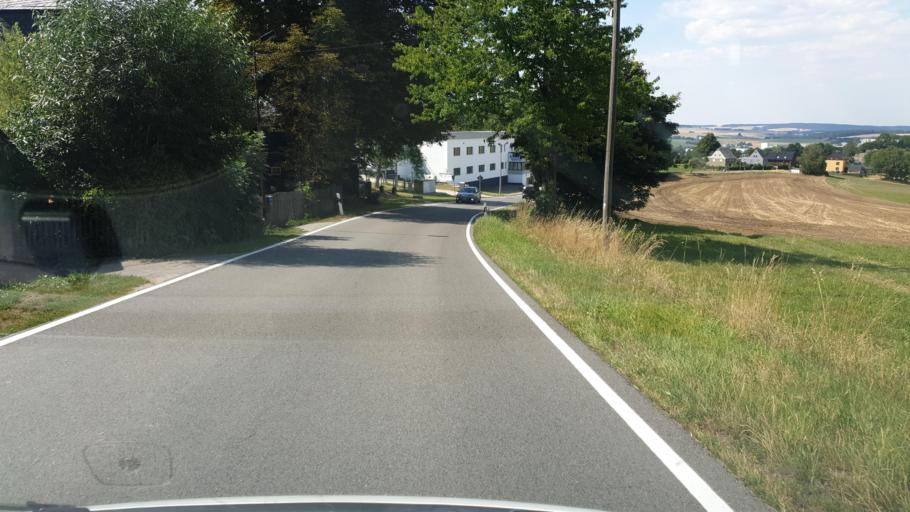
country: DE
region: Saxony
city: Zschopau
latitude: 50.7273
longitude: 13.0864
